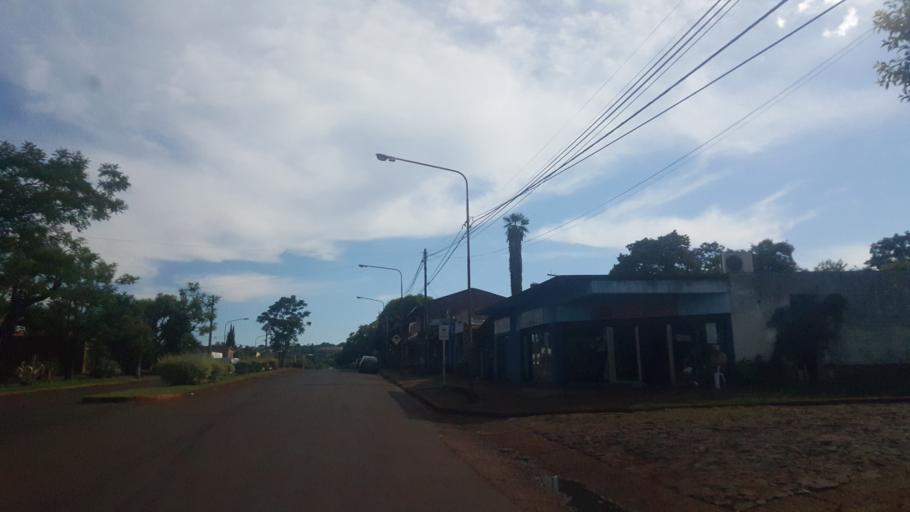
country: AR
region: Misiones
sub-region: Departamento de Leandro N. Alem
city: Leandro N. Alem
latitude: -27.5945
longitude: -55.3233
